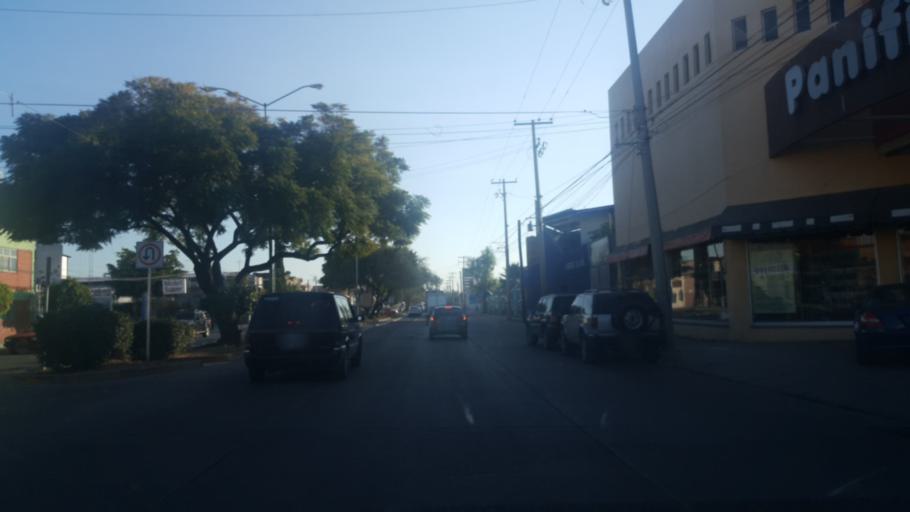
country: MX
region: Guanajuato
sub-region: Leon
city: Medina
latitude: 21.1140
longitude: -101.6346
